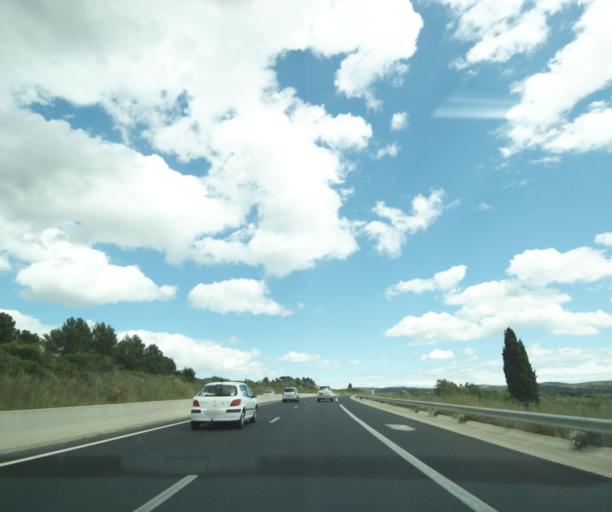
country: FR
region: Languedoc-Roussillon
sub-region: Departement de l'Herault
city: Gignac
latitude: 43.6442
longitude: 3.5621
